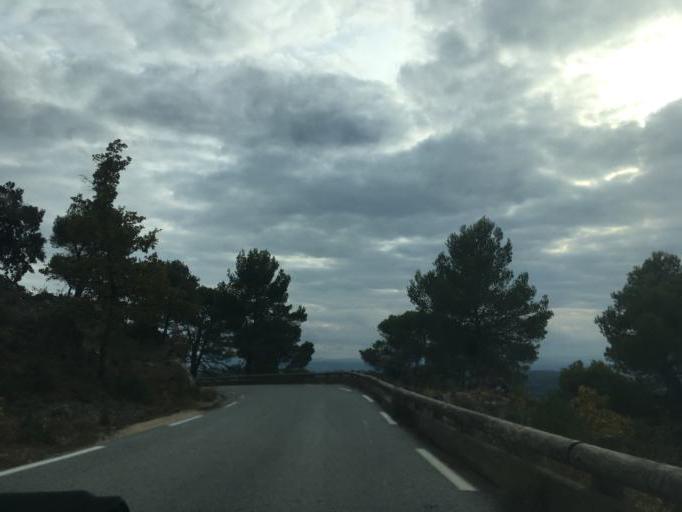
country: FR
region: Provence-Alpes-Cote d'Azur
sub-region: Departement du Var
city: Villecroze
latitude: 43.5821
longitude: 6.3102
